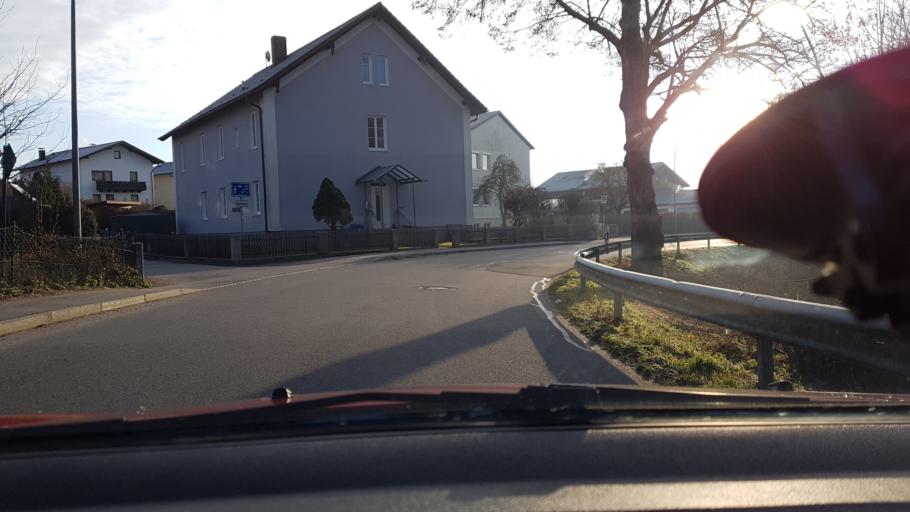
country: DE
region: Bavaria
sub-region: Lower Bavaria
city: Stubenberg
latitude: 48.2889
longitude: 13.0763
